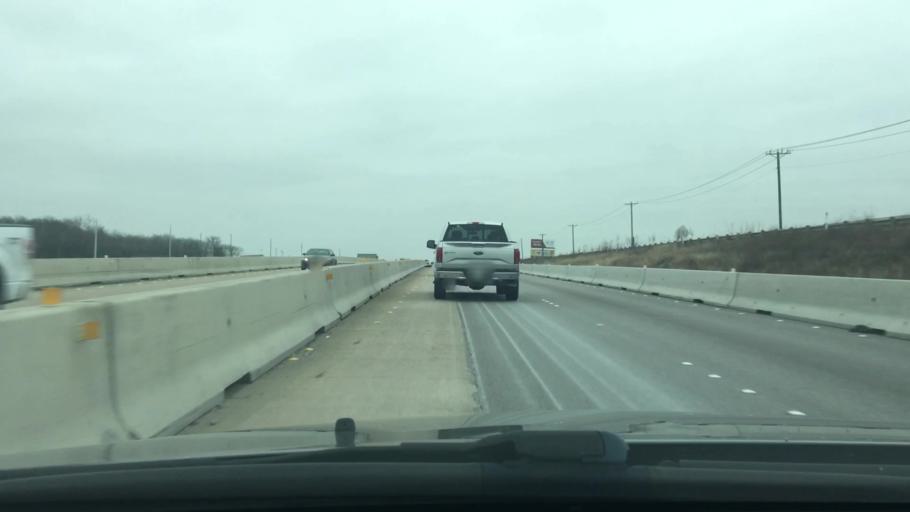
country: US
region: Texas
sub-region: Navarro County
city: Corsicana
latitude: 32.0383
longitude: -96.4460
